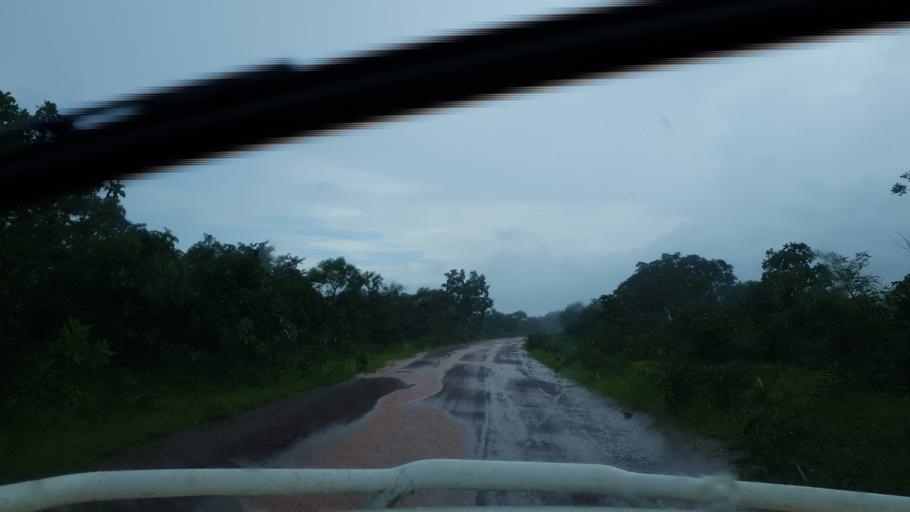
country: ML
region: Sikasso
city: Kolondieba
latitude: 11.6027
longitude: -6.6721
